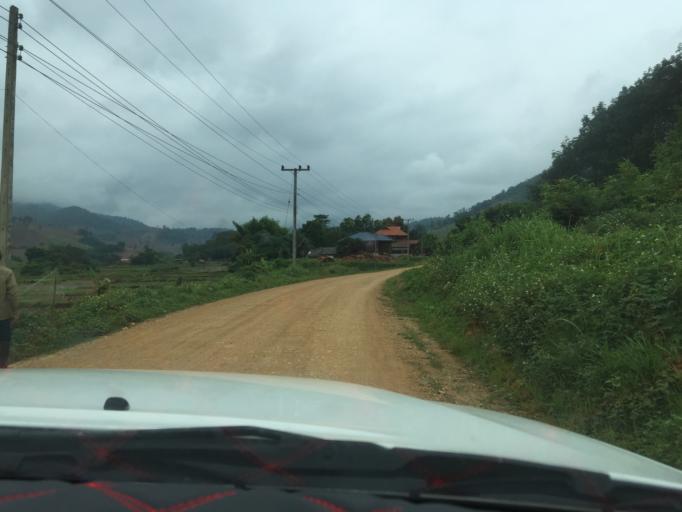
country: TH
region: Phayao
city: Phu Sang
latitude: 19.6906
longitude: 100.5021
